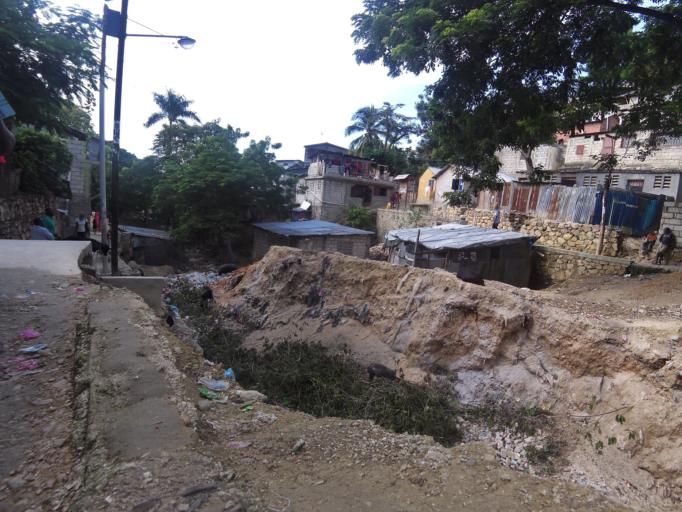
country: HT
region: Ouest
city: Port-au-Prince
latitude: 18.5236
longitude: -72.3339
